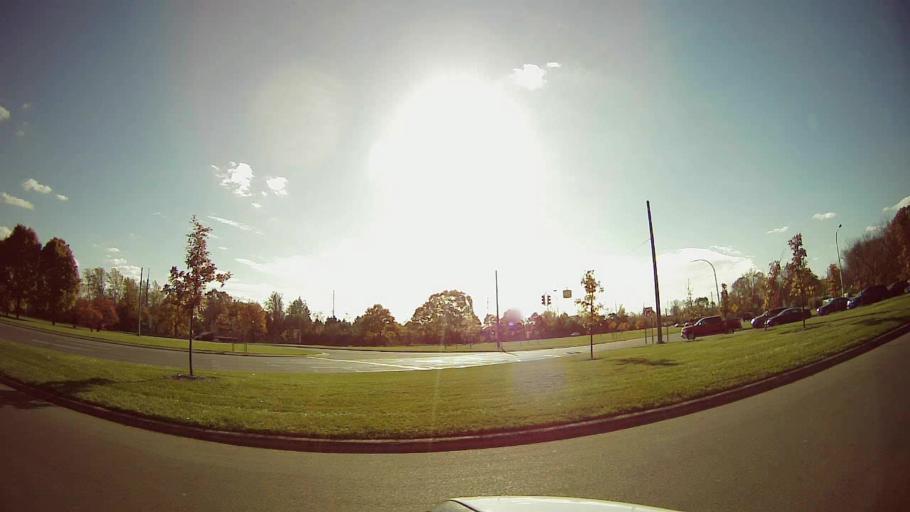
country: US
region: Michigan
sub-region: Wayne County
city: Dearborn
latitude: 42.3094
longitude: -83.2255
